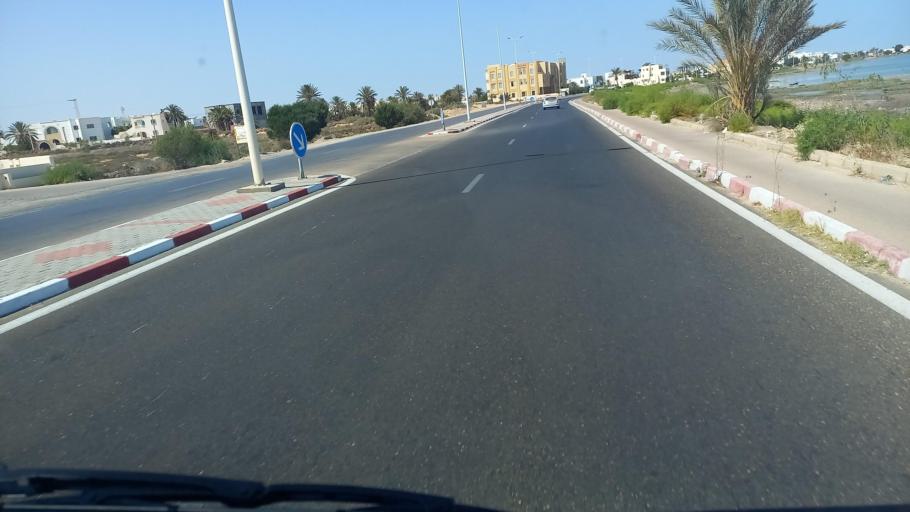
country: TN
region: Madanin
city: Houmt Souk
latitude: 33.8742
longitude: 10.9008
